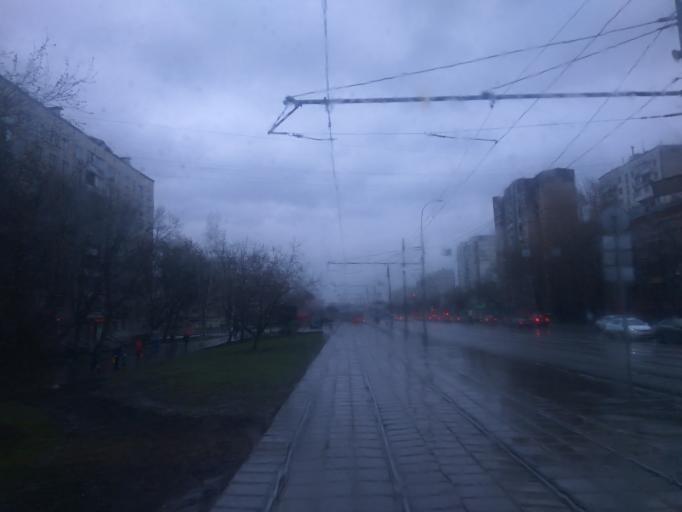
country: RU
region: Moscow
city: Leonovo
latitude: 55.8675
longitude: 37.6631
